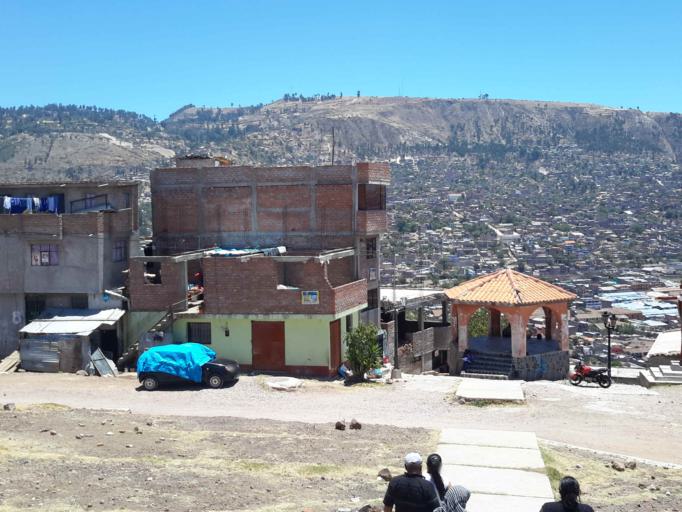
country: PE
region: Ayacucho
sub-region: Provincia de Huamanga
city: Carmen Alto
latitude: -13.1710
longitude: -74.2223
